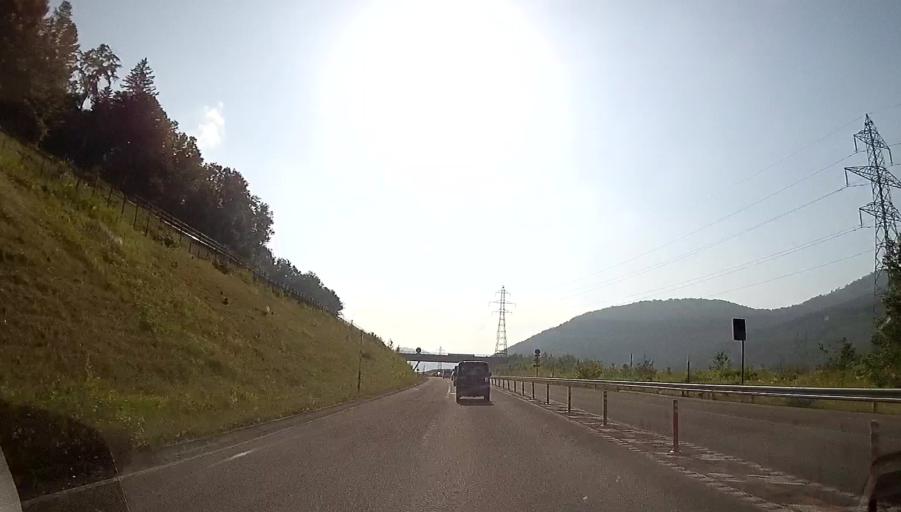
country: JP
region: Hokkaido
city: Shimo-furano
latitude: 43.0541
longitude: 142.6081
